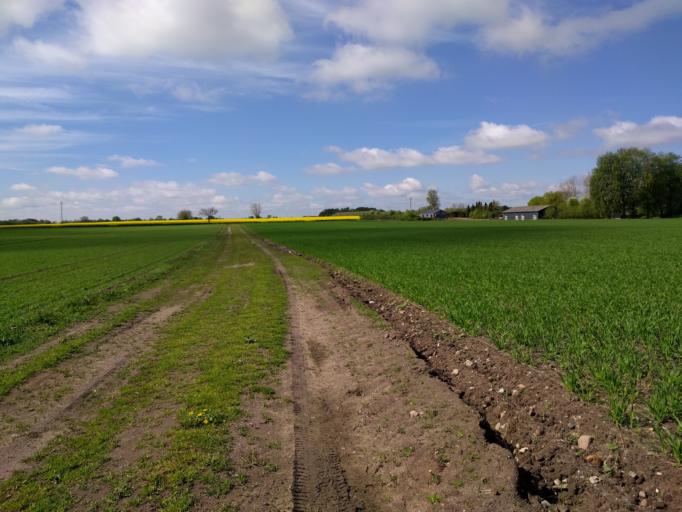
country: DK
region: South Denmark
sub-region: Kerteminde Kommune
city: Langeskov
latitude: 55.3930
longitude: 10.5729
